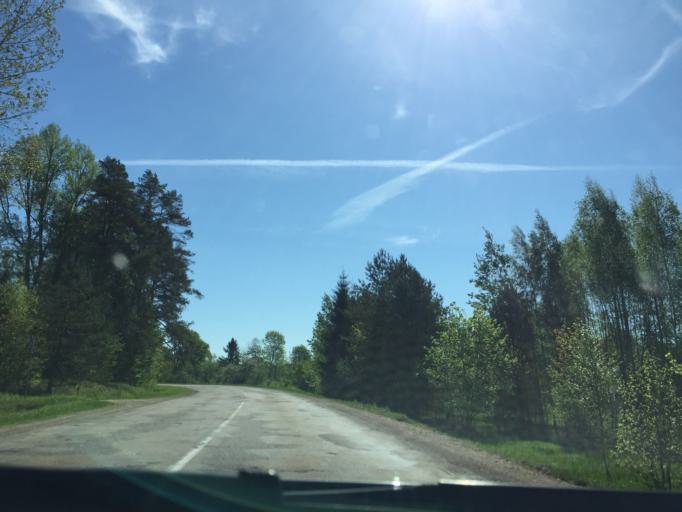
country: LV
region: Ropazu
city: Ropazi
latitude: 57.0069
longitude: 24.5734
